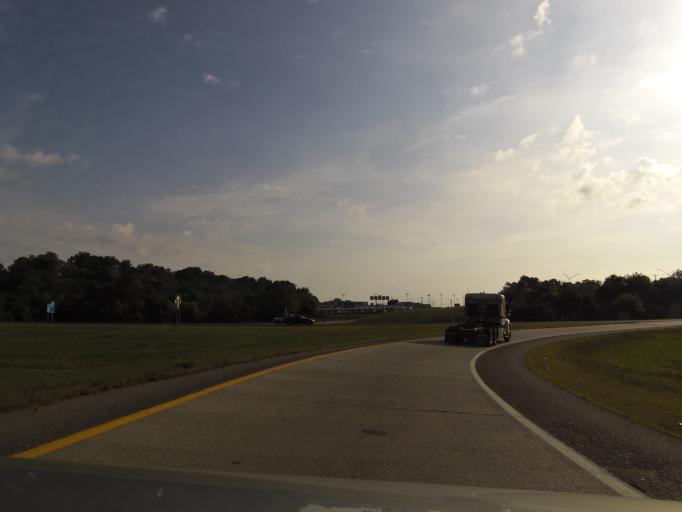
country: US
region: Tennessee
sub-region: Blount County
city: Alcoa
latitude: 35.8359
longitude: -83.9728
